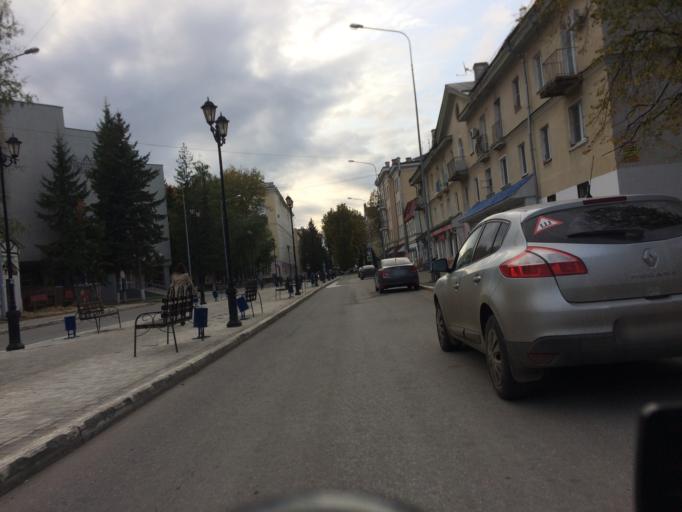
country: RU
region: Mariy-El
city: Yoshkar-Ola
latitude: 56.6303
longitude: 47.8962
